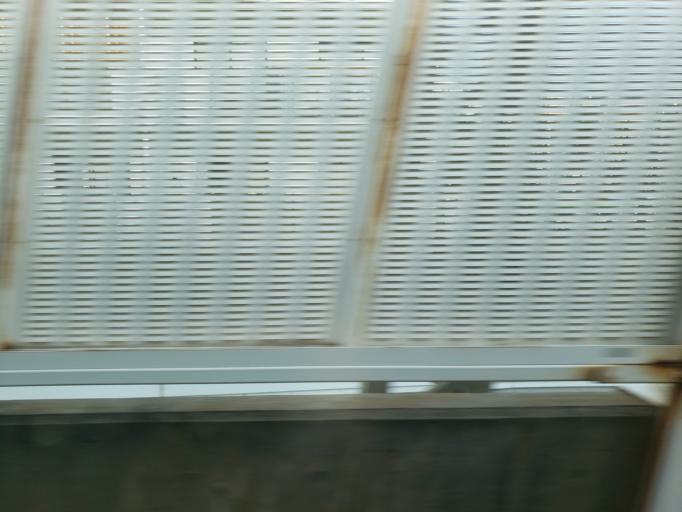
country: JP
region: Hyogo
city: Ashiya
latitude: 34.7306
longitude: 135.2918
